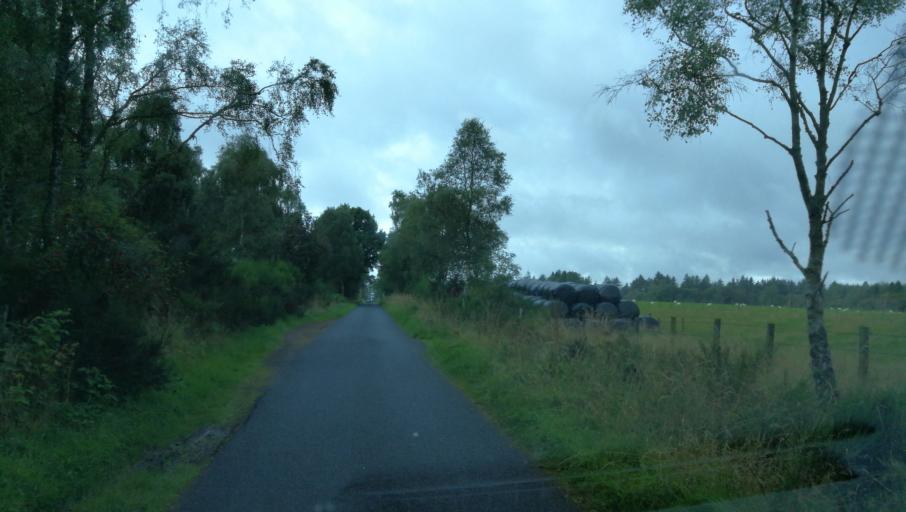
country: GB
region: Scotland
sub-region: Perth and Kinross
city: Alyth
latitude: 56.6196
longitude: -3.2795
